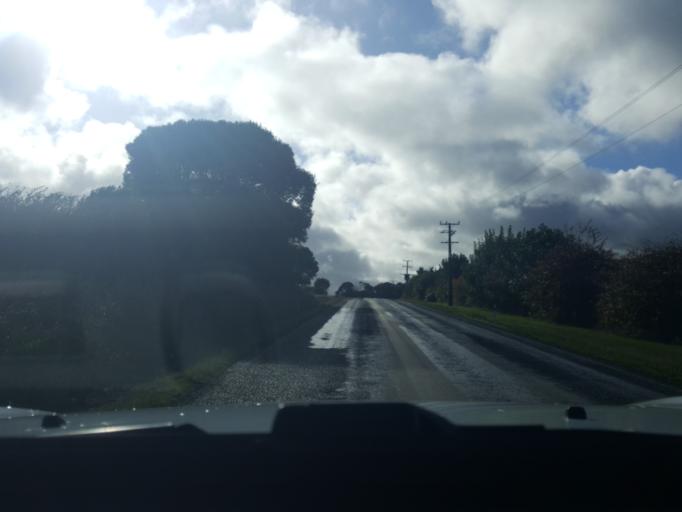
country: NZ
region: Auckland
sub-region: Auckland
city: Pukekohe East
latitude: -37.3026
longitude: 175.0184
